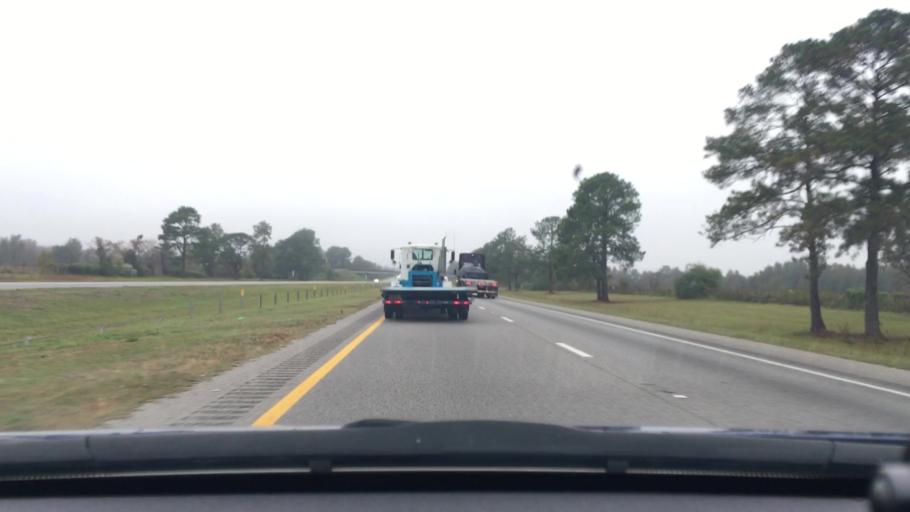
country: US
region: South Carolina
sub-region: Lee County
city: Bishopville
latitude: 34.1894
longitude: -80.2443
